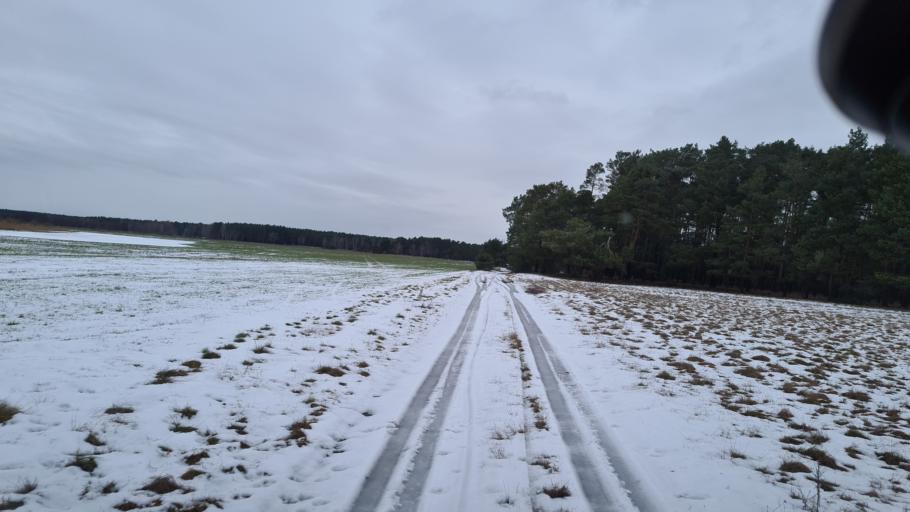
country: DE
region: Brandenburg
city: Schenkendobern
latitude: 51.9027
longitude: 14.5946
